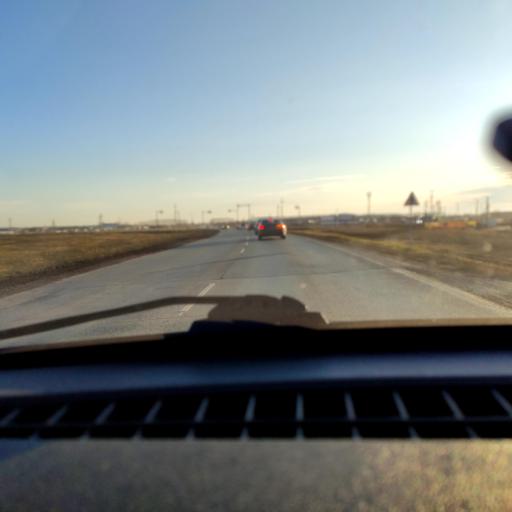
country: RU
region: Bashkortostan
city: Ufa
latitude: 54.6273
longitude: 55.8945
